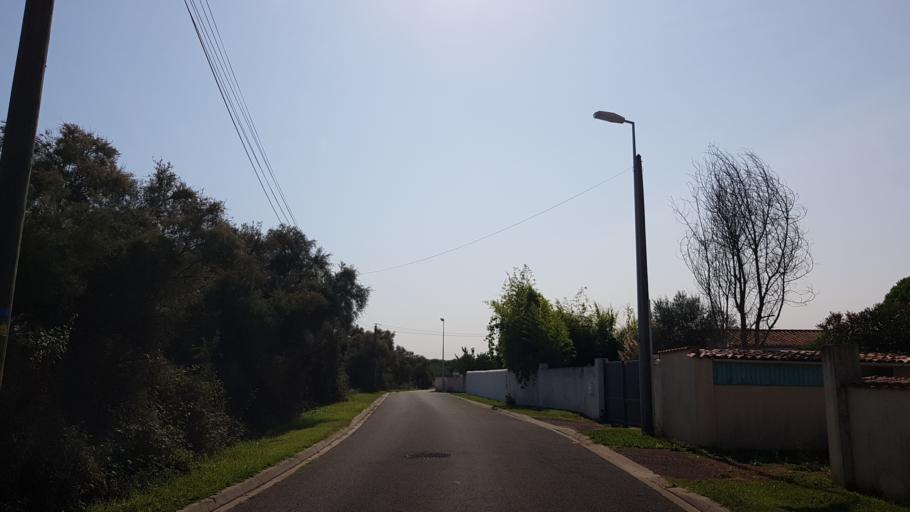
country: FR
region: Poitou-Charentes
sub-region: Departement de la Charente-Maritime
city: Breuillet
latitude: 45.7059
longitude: -1.0249
